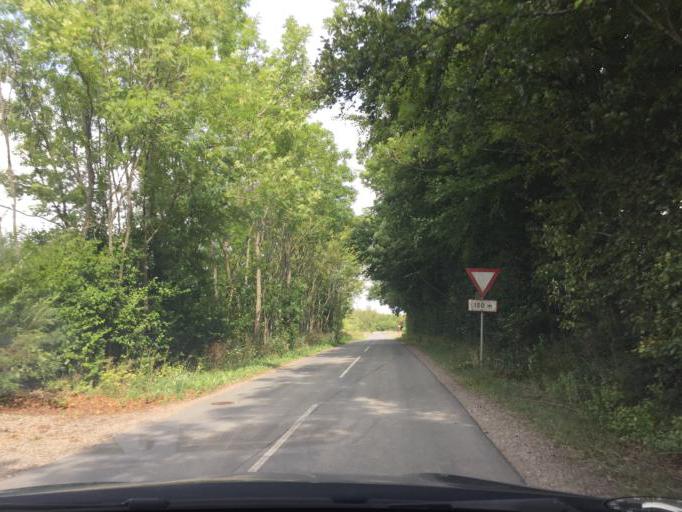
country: DK
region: South Denmark
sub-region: Assens Kommune
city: Tommerup Stationsby
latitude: 55.3854
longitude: 10.1780
